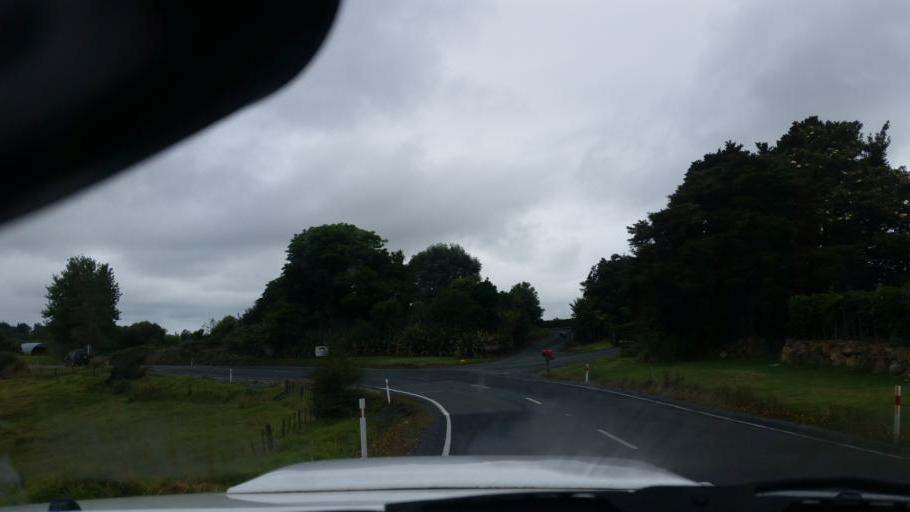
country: NZ
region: Auckland
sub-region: Auckland
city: Wellsford
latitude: -36.1516
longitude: 174.4732
